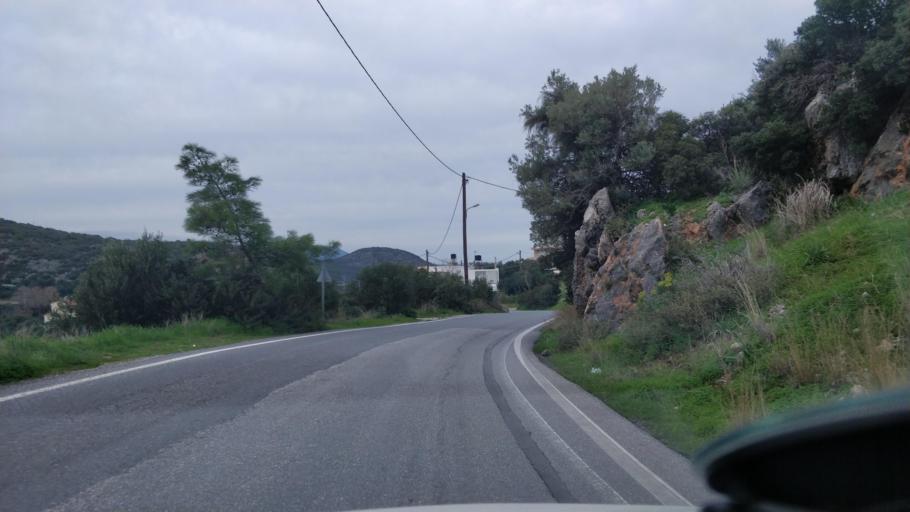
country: GR
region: Crete
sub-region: Nomos Lasithiou
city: Agios Nikolaos
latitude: 35.1185
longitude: 25.7268
